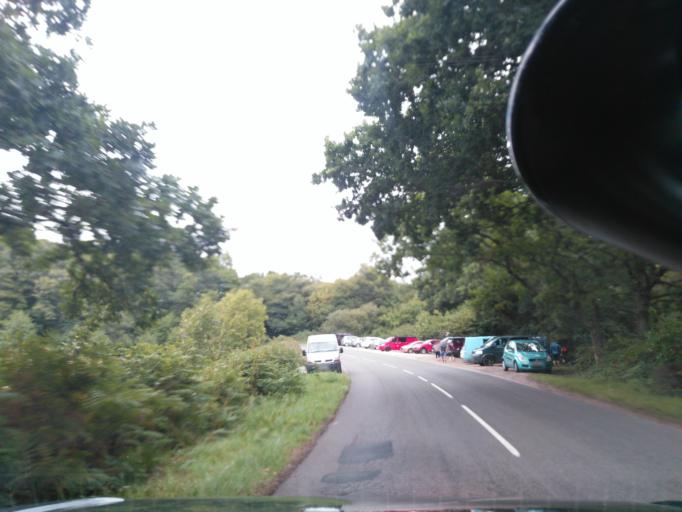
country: GB
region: England
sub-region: Dorset
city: Wareham
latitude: 50.7325
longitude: -2.1159
